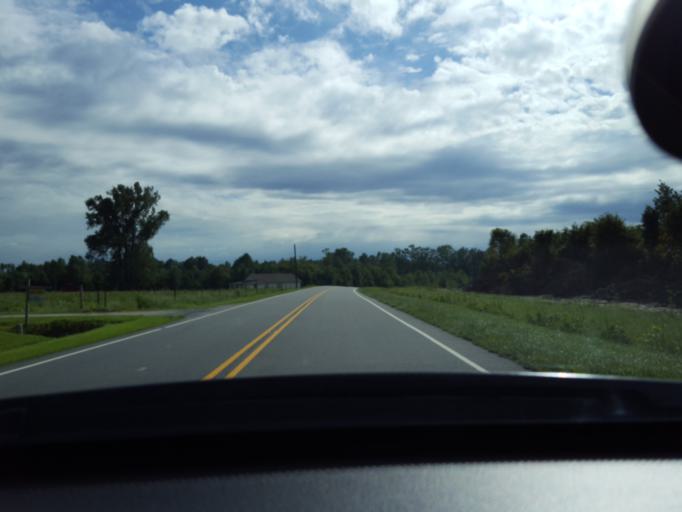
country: US
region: North Carolina
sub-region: Duplin County
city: Kenansville
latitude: 34.9962
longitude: -77.9225
